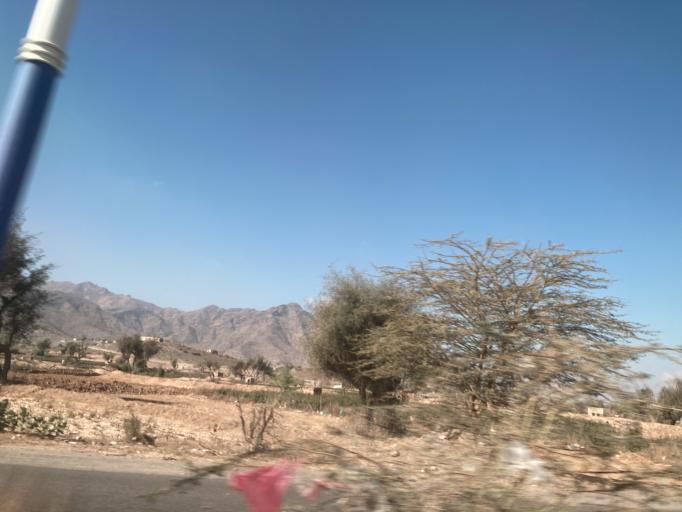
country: YE
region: Ad Dali'
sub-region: Al Hussein
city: Al Husayn
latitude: 13.8059
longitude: 44.7252
